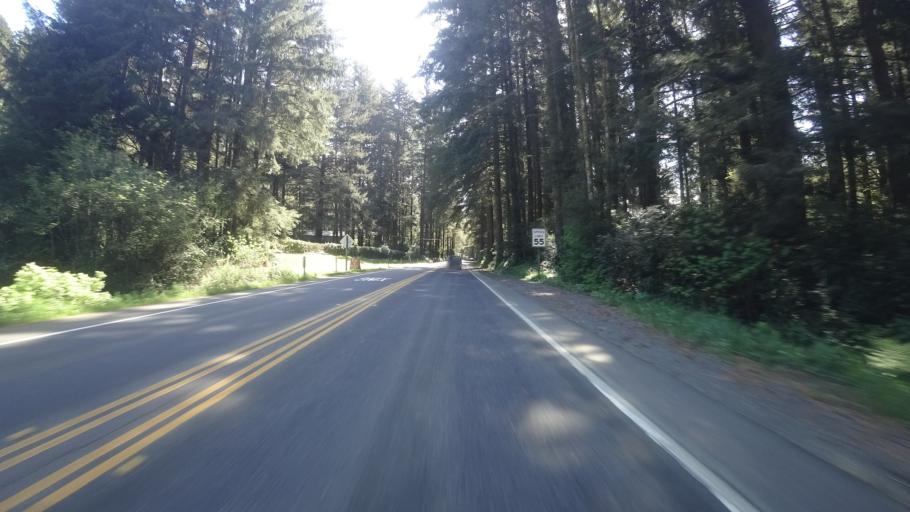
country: US
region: California
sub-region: Del Norte County
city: Bertsch-Oceanview
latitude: 41.5837
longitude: -124.0851
